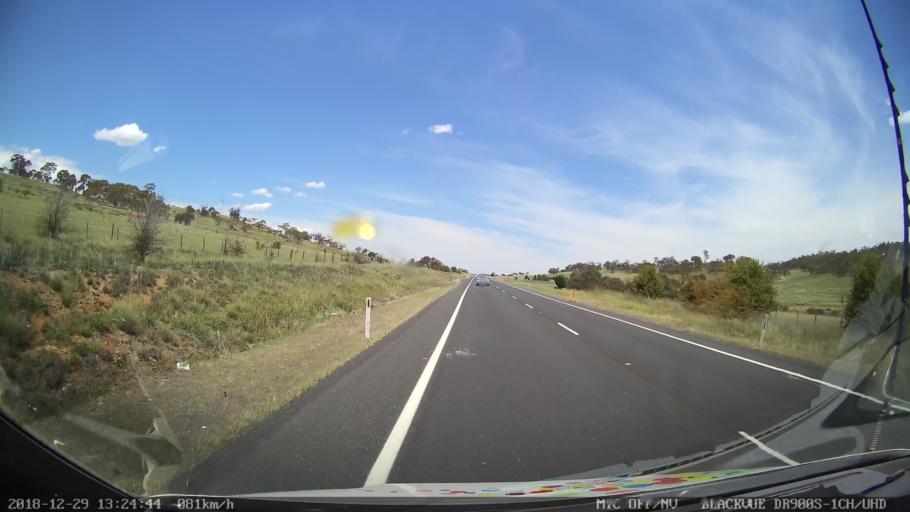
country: AU
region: New South Wales
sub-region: Cooma-Monaro
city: Cooma
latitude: -35.8335
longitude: 149.1622
